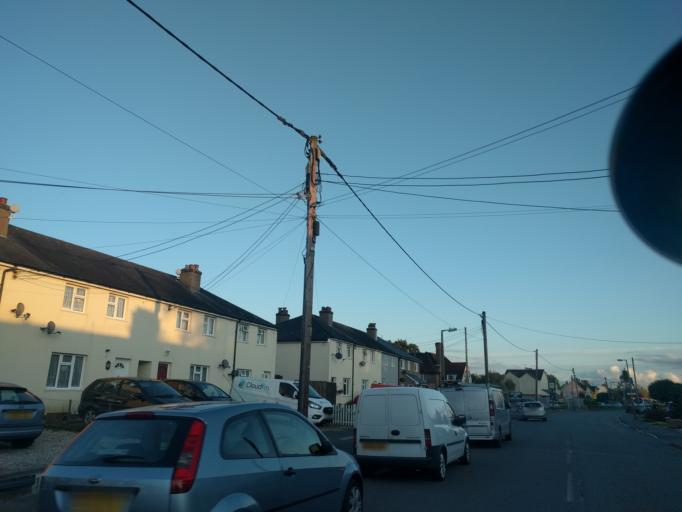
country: GB
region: England
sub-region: Essex
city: Rayne
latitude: 51.8767
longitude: 0.5729
